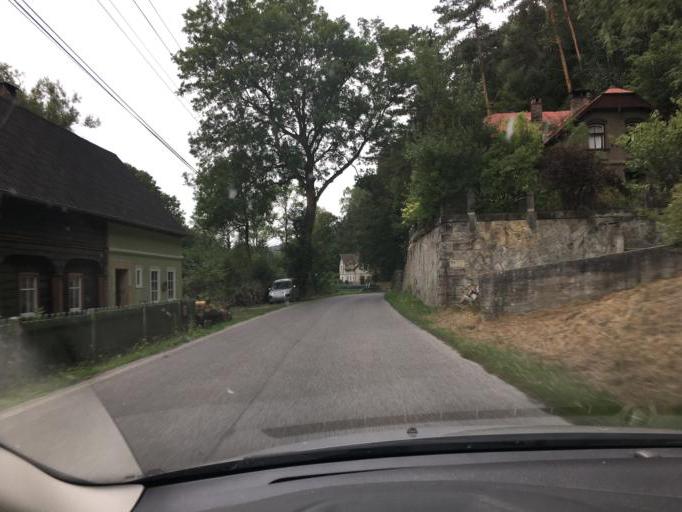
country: CZ
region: Ustecky
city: Ceska Kamenice
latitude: 50.8101
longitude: 14.3581
